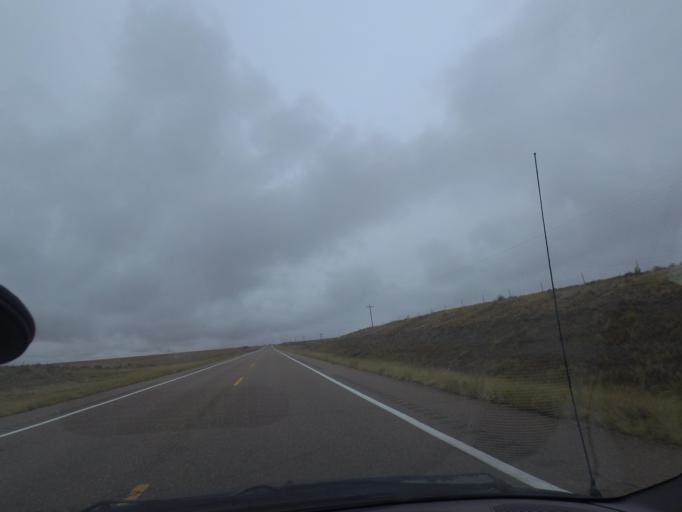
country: US
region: Colorado
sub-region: Arapahoe County
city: Byers
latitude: 39.7399
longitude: -103.7544
